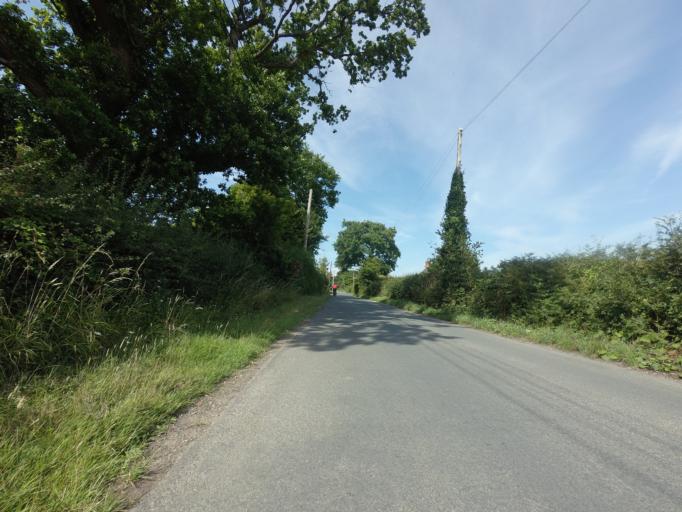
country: GB
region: England
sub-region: East Sussex
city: Rye
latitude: 50.9761
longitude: 0.7403
